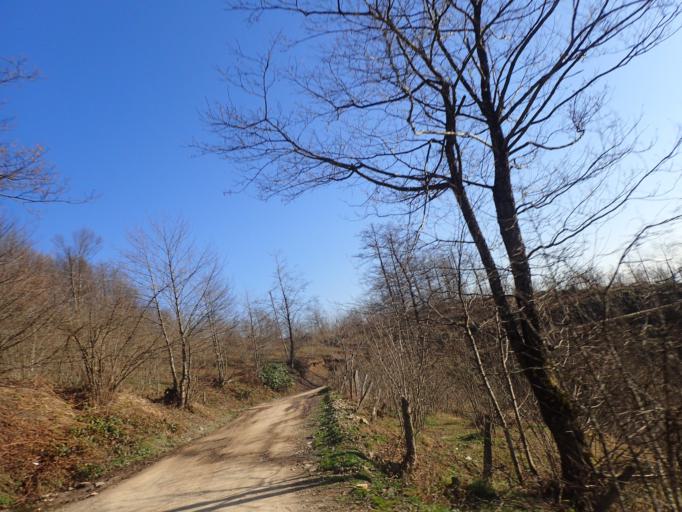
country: TR
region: Ordu
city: Camas
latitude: 40.8534
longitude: 37.5058
